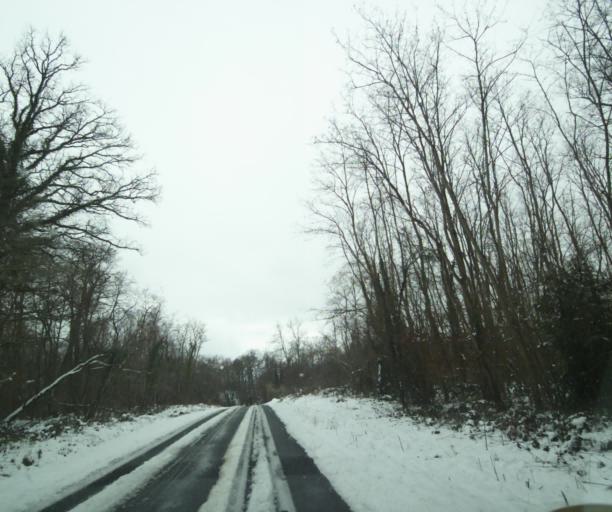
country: FR
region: Champagne-Ardenne
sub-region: Departement de la Haute-Marne
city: Montier-en-Der
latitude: 48.4225
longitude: 4.7284
